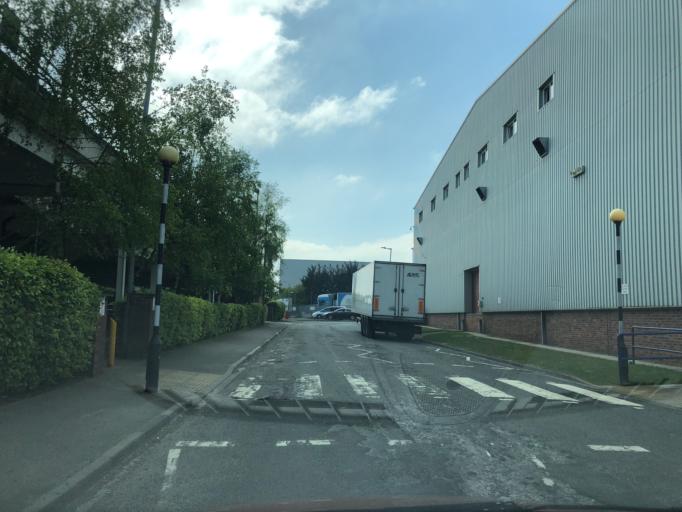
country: GB
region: England
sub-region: North Yorkshire
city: Bedale
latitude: 54.3046
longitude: -1.5643
